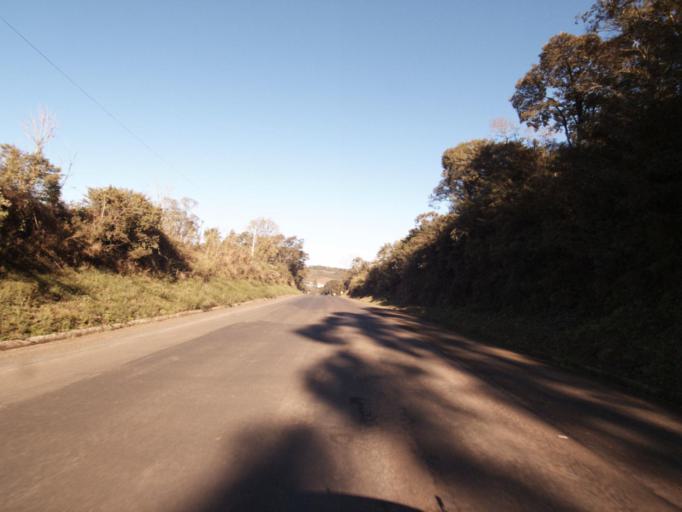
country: BR
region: Rio Grande do Sul
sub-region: Frederico Westphalen
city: Frederico Westphalen
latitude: -26.8920
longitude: -53.1865
